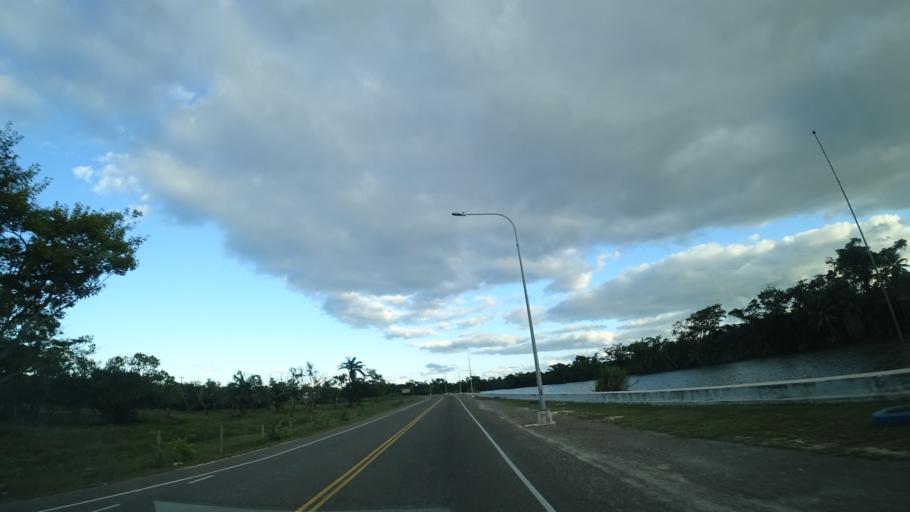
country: BZ
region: Belize
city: Belize City
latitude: 17.5430
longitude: -88.2646
